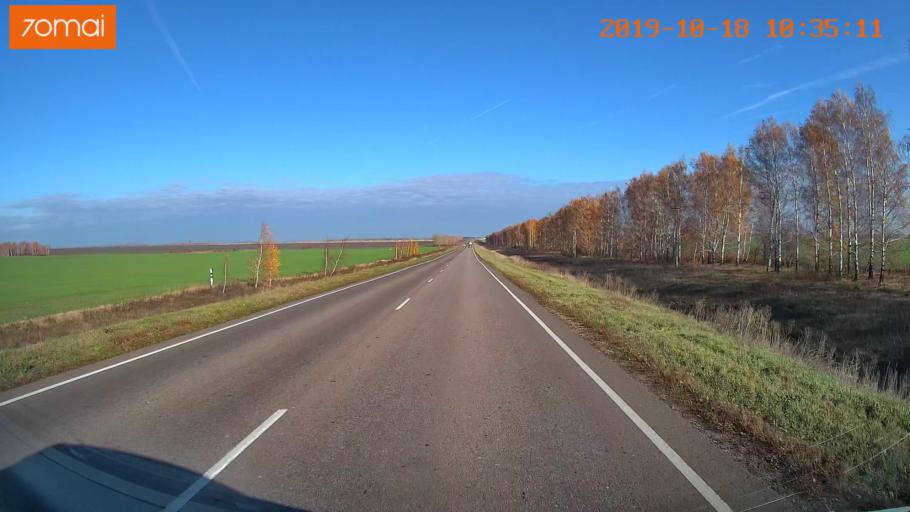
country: RU
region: Tula
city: Kurkino
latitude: 53.5292
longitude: 38.6184
